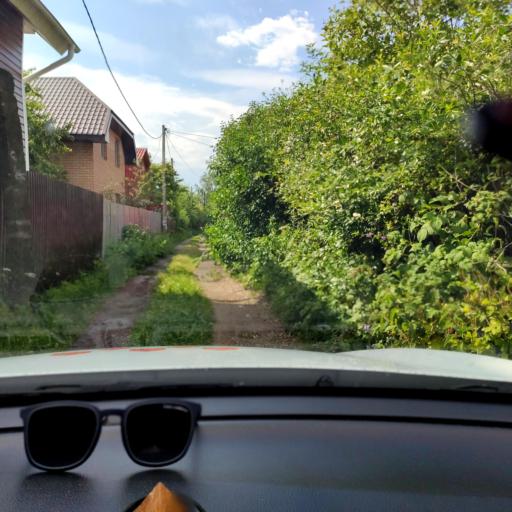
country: RU
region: Tatarstan
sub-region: Zelenodol'skiy Rayon
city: Vasil'yevo
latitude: 55.8225
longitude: 48.7248
